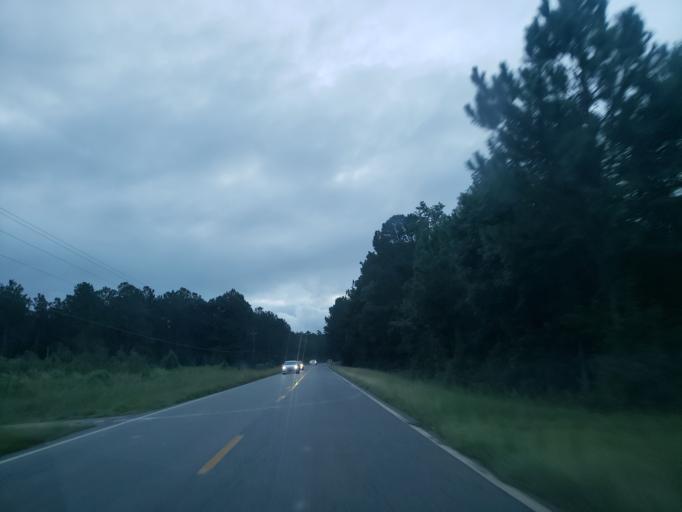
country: US
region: Georgia
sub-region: Chatham County
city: Pooler
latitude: 32.0539
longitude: -81.2935
